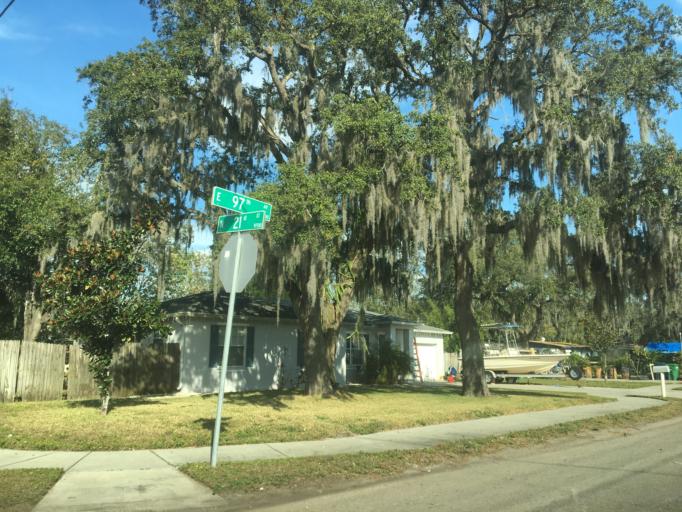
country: US
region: Florida
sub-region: Hillsborough County
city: University
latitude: 28.0373
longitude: -82.4359
